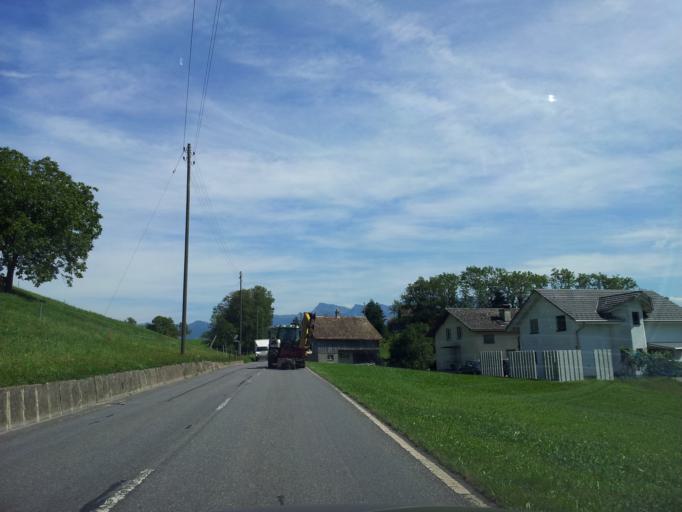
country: CH
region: Schwyz
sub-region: Bezirk March
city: Schubelbach
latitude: 47.1918
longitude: 8.9269
